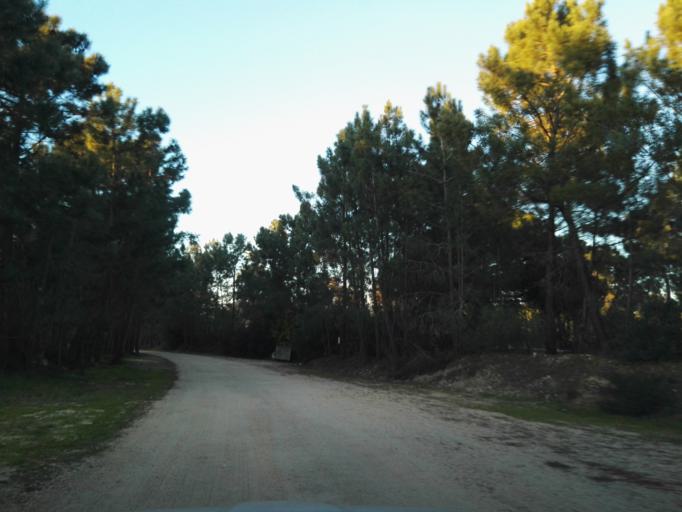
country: PT
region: Setubal
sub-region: Seixal
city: Corroios
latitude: 38.6166
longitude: -9.1473
